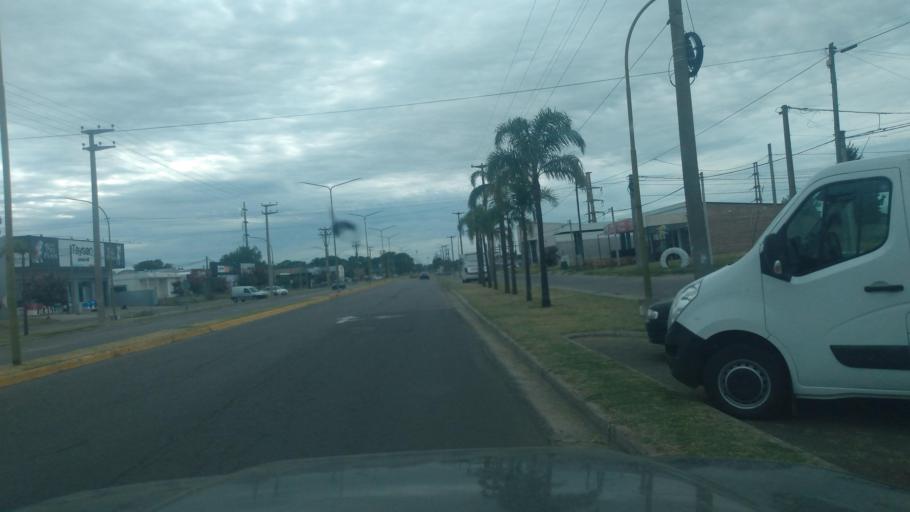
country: AR
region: Buenos Aires
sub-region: Partido de Trenque Lauquen
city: Trenque Lauquen
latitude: -35.9833
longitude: -62.7259
